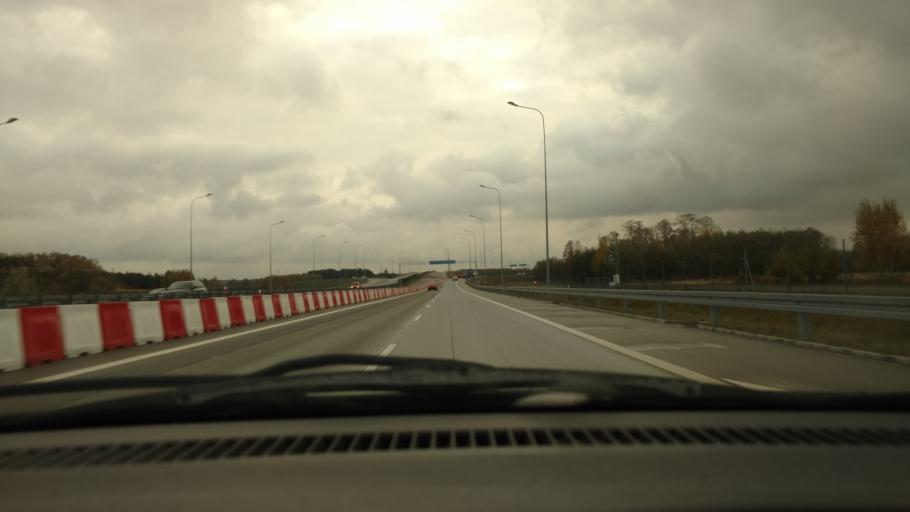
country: PL
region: Lodz Voivodeship
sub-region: Powiat lodzki wschodni
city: Tuszyn
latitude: 51.6402
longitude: 19.5616
